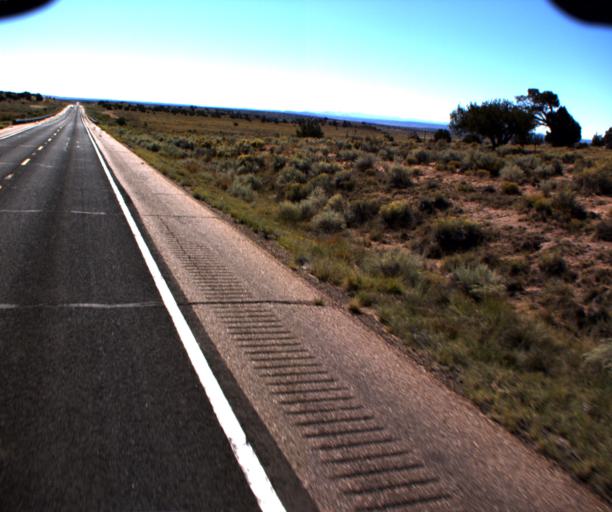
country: US
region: Arizona
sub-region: Navajo County
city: Snowflake
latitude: 34.6798
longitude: -109.7335
